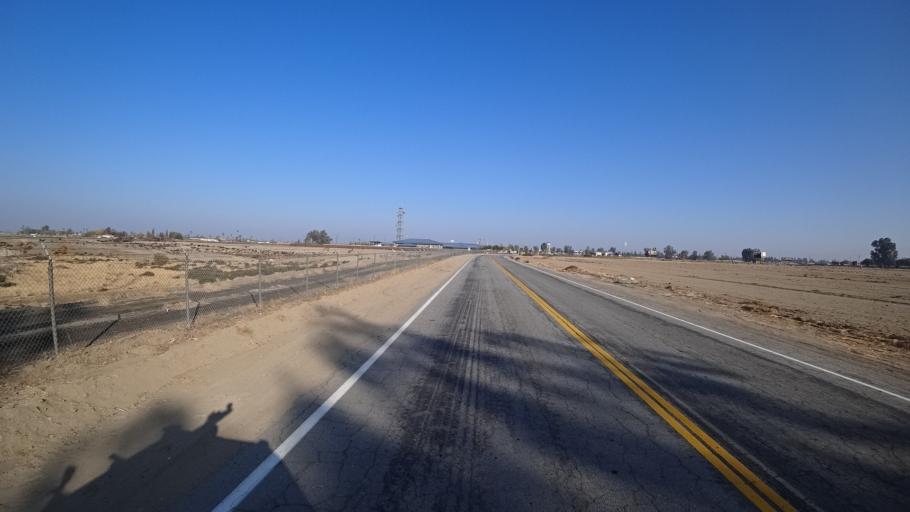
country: US
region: California
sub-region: Kern County
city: Greenfield
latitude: 35.2617
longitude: -119.0258
